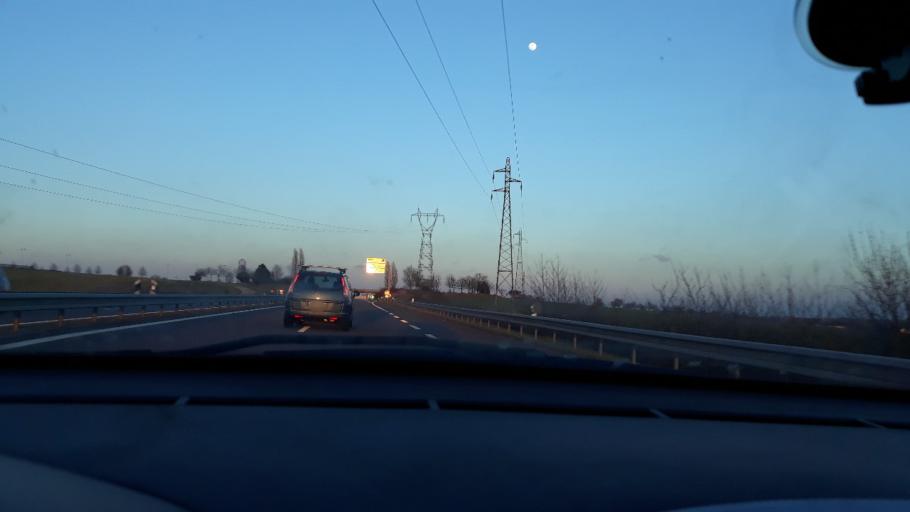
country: FR
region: Lorraine
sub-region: Departement de la Moselle
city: OEting
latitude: 49.1614
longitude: 6.9121
